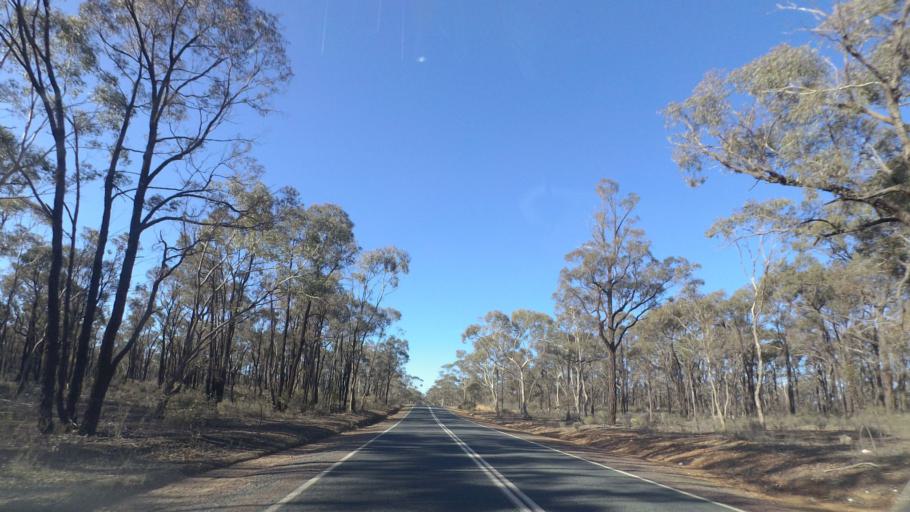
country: AU
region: Victoria
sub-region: Greater Bendigo
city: Epsom
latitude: -36.6680
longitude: 144.4280
